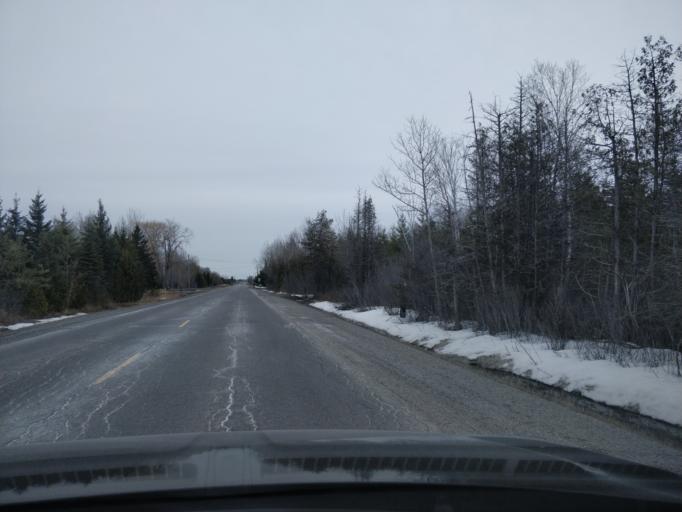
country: CA
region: Ontario
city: Bells Corners
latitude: 45.2431
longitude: -75.8936
